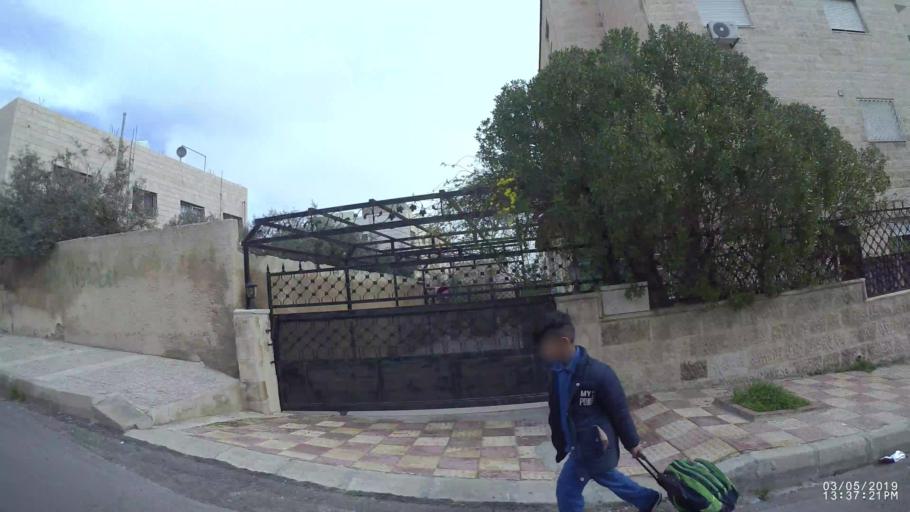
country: JO
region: Amman
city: Amman
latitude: 31.9969
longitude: 35.9414
